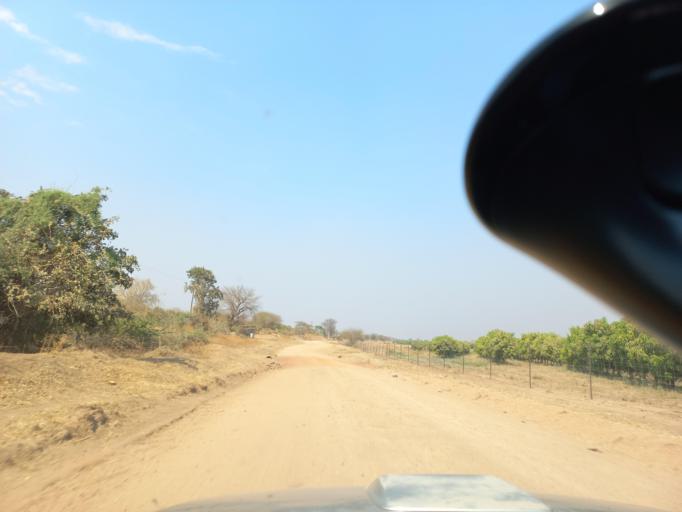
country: ZW
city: Chirundu
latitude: -15.9319
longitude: 28.9512
